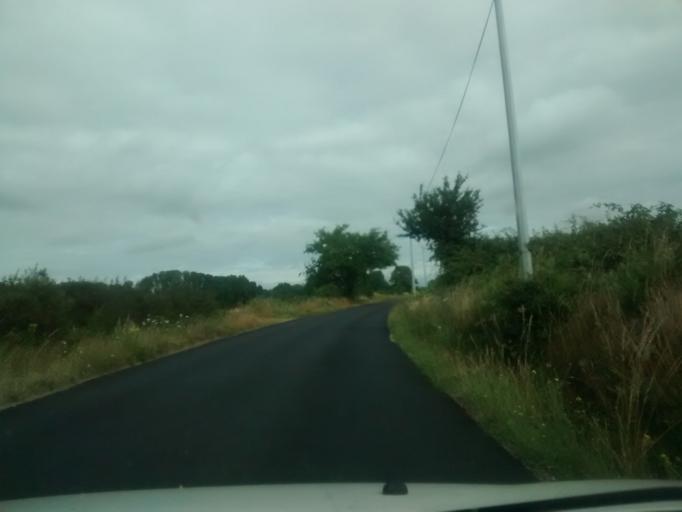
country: FR
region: Brittany
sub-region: Departement d'Ille-et-Vilaine
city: Saint-Jacques-de-la-Lande
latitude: 48.0880
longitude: -1.7368
